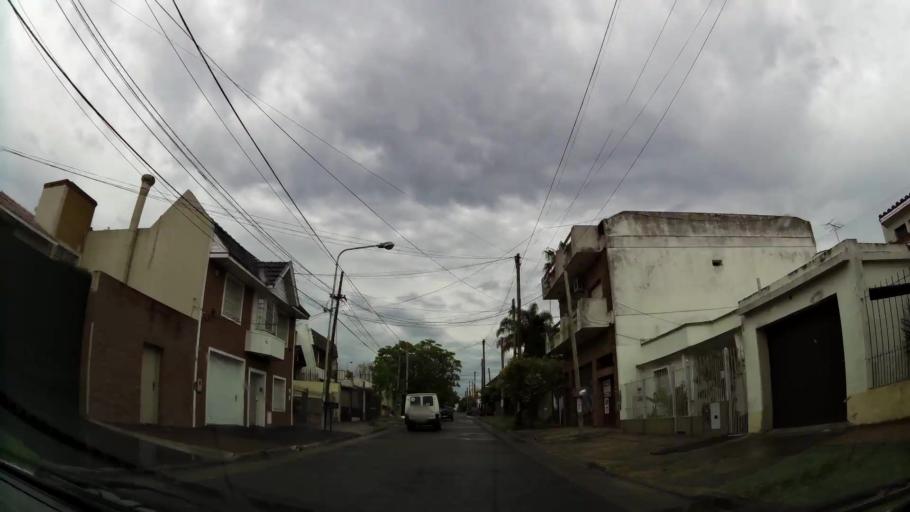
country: AR
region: Buenos Aires
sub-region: Partido de Quilmes
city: Quilmes
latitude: -34.7653
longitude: -58.2189
